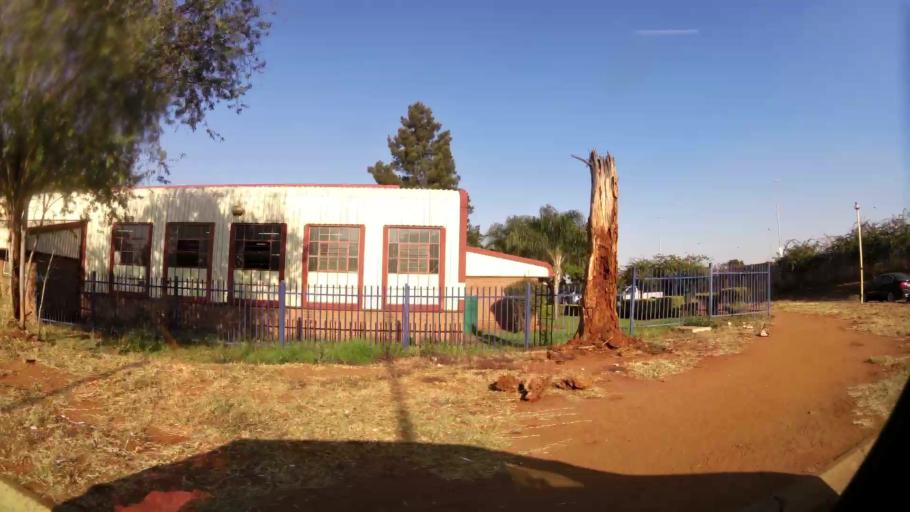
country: ZA
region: North-West
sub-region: Bojanala Platinum District Municipality
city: Rustenburg
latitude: -25.6498
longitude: 27.2155
